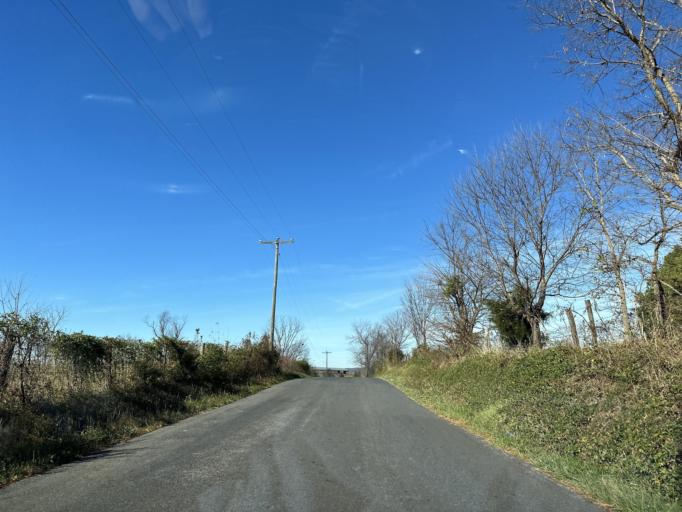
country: US
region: Virginia
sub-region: Augusta County
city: Weyers Cave
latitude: 38.2171
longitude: -78.9155
